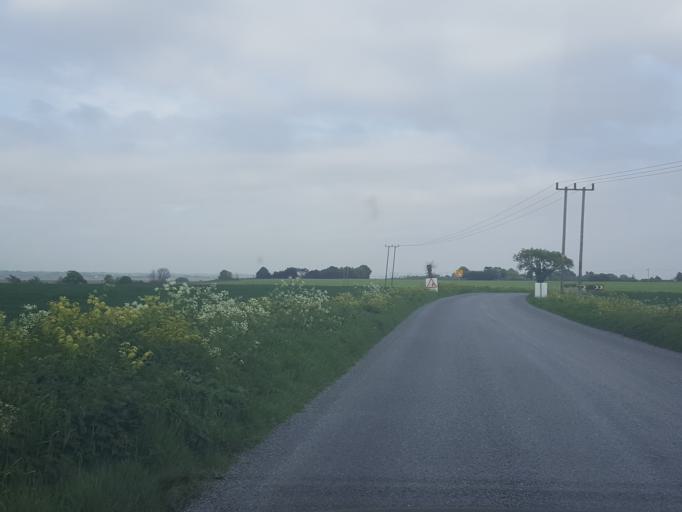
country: GB
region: England
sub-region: Essex
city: Frinton-on-Sea
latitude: 51.8519
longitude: 1.1938
